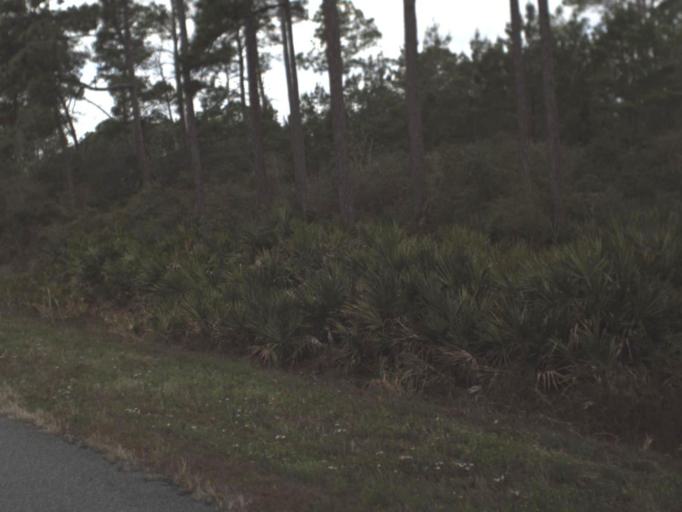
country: US
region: Florida
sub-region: Franklin County
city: Carrabelle
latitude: 29.7930
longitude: -84.7515
